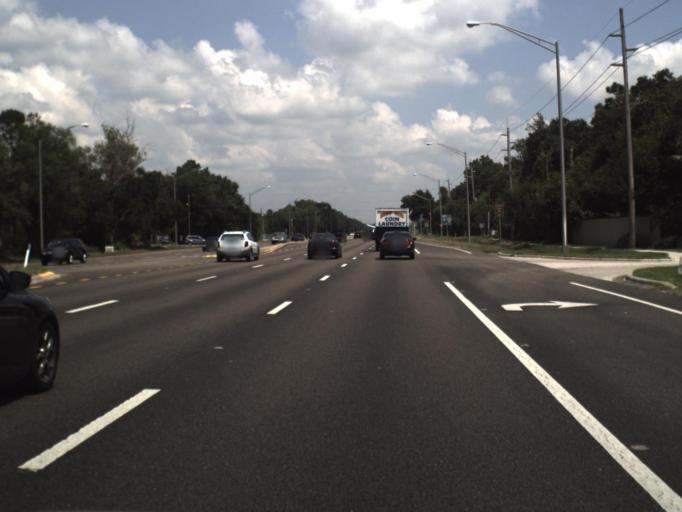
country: US
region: Florida
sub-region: Hillsborough County
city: Greater Northdale
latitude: 28.1172
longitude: -82.5024
